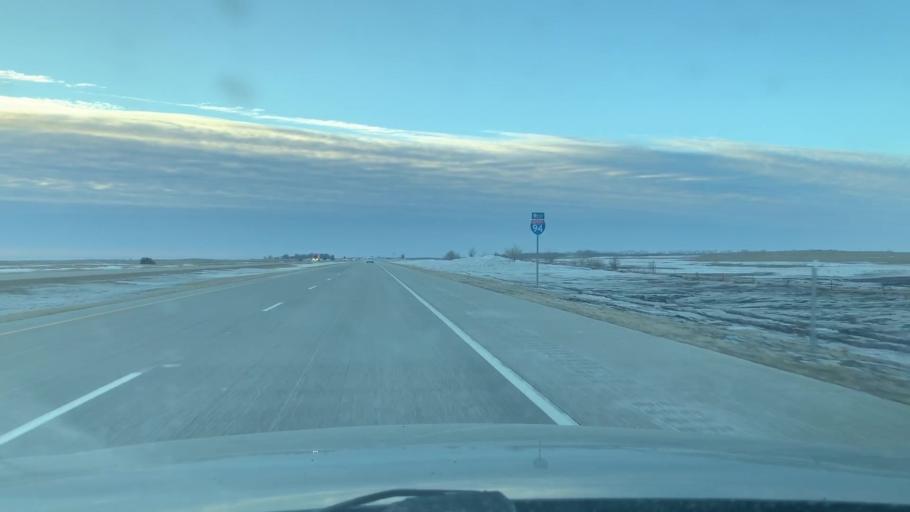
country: US
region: North Dakota
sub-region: Ransom County
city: Sheldon
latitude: 46.8758
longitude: -97.5029
